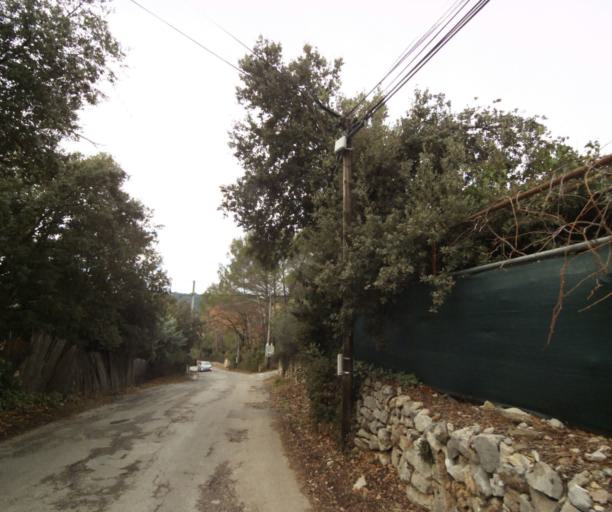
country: FR
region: Provence-Alpes-Cote d'Azur
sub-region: Departement du Var
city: Trans-en-Provence
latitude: 43.5080
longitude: 6.4914
